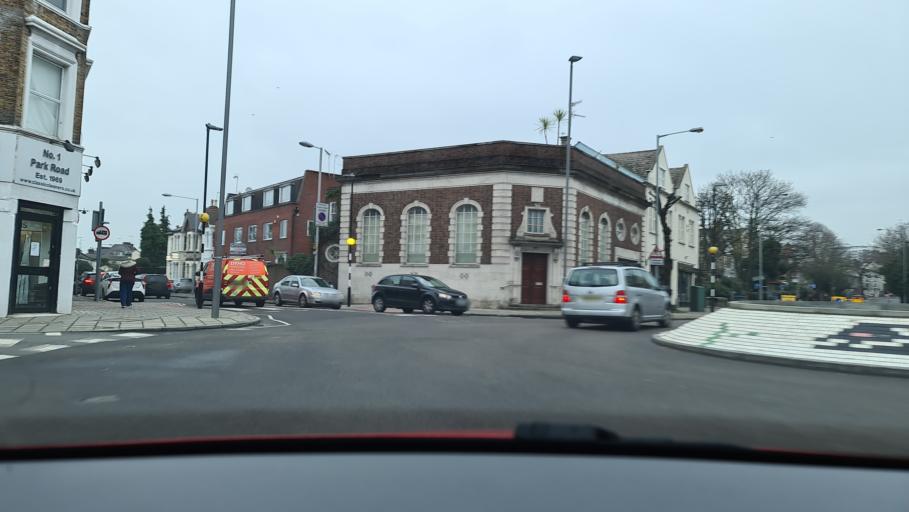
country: GB
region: England
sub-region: Greater London
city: Kingston upon Thames
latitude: 51.4137
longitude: -0.2876
